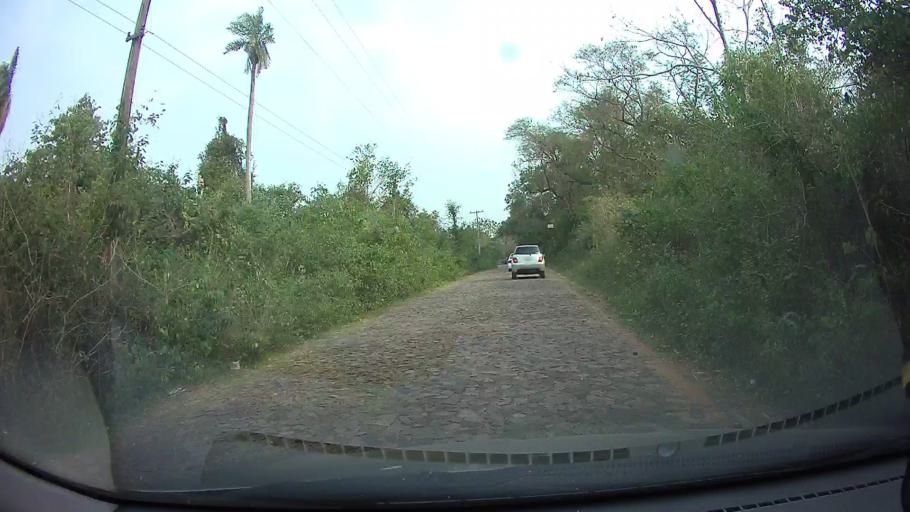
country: PY
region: Cordillera
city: Arroyos y Esteros
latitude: -25.0308
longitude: -57.1098
